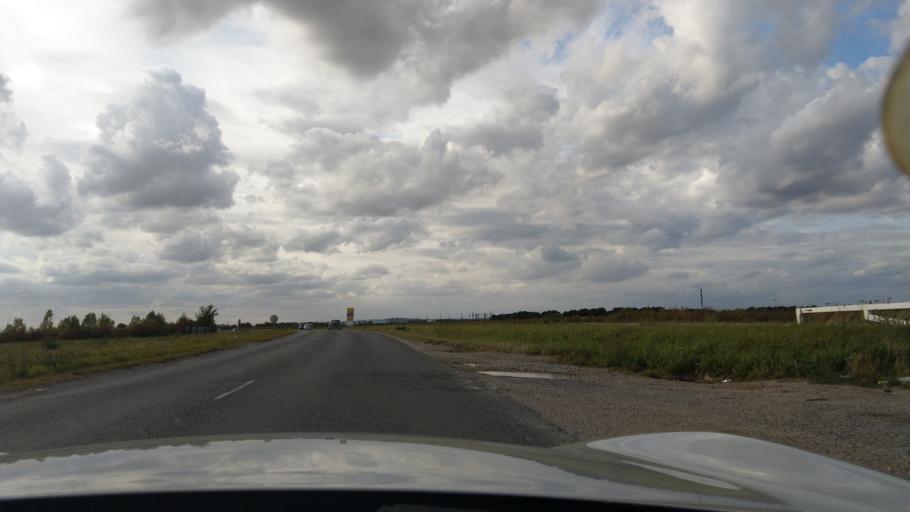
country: FR
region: Ile-de-France
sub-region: Departement du Val-d'Oise
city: Vemars
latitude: 49.0296
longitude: 2.5772
